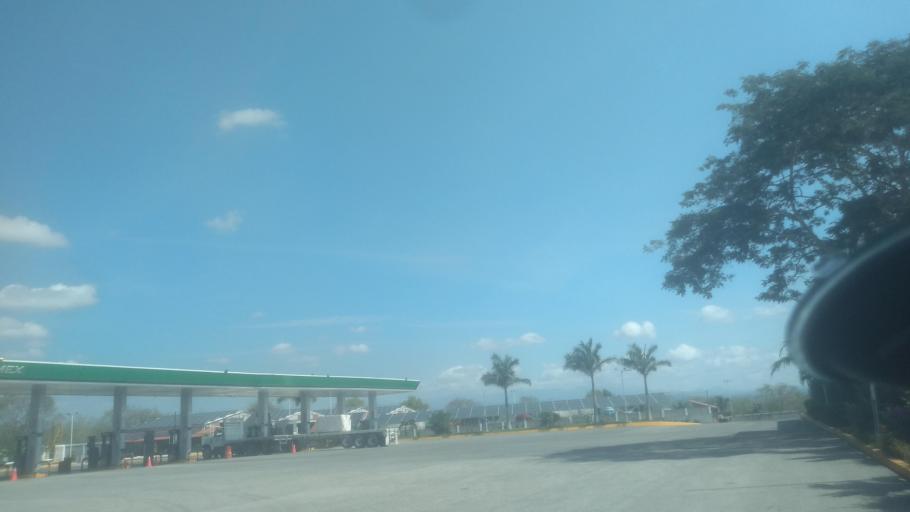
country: MX
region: Veracruz
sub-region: Emiliano Zapata
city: Plan del Rio
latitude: 19.3931
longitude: -96.6277
